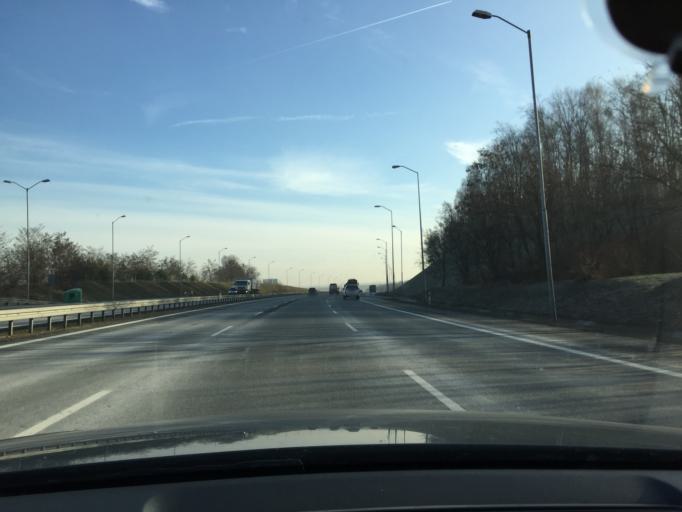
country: PL
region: Silesian Voivodeship
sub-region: Ruda Slaska
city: Ruda Slaska
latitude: 50.2515
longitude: 18.8831
